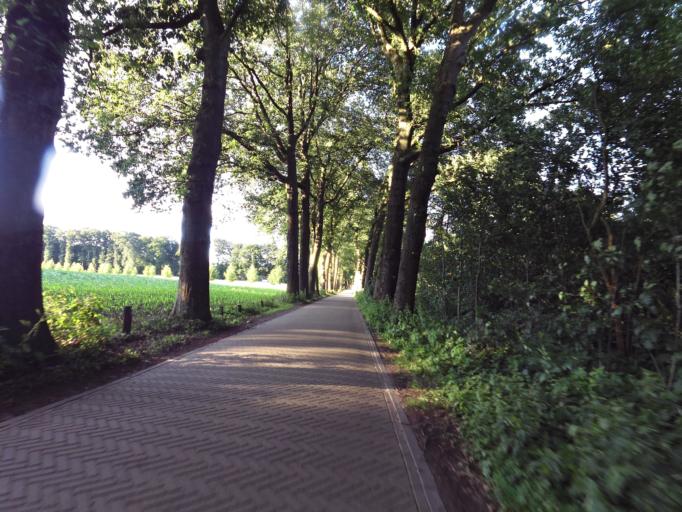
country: NL
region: Gelderland
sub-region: Gemeente Doetinchem
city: Doetinchem
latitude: 51.9755
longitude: 6.2815
